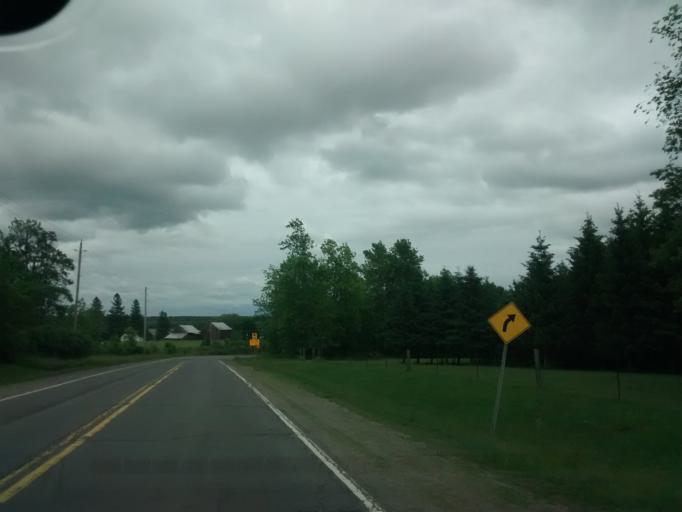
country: CA
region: Ontario
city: Brockville
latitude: 44.6394
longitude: -75.6124
